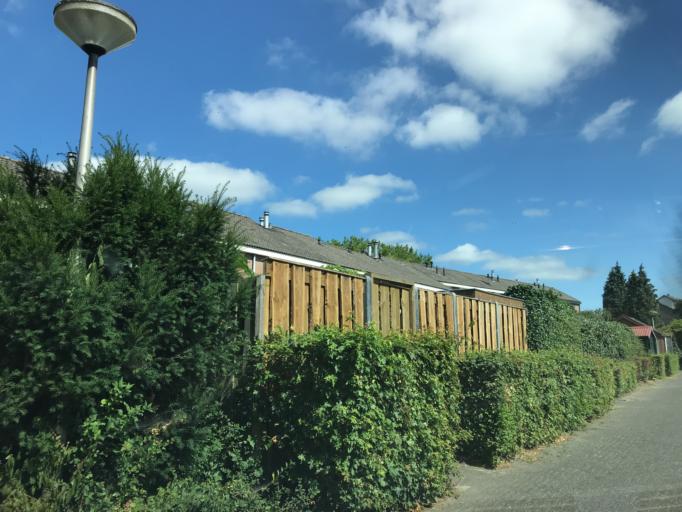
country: NL
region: North Holland
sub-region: Gemeente Huizen
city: Huizen
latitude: 52.2972
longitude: 5.2567
